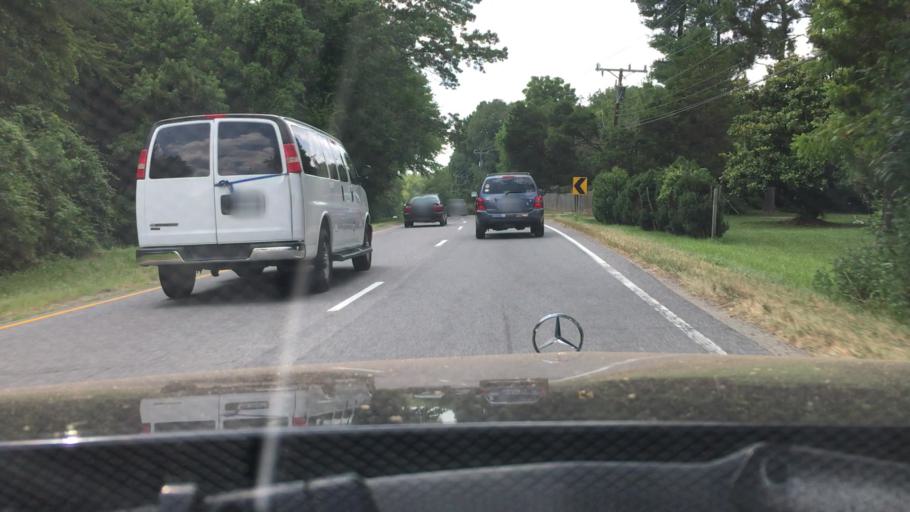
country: US
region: Virginia
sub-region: Spotsylvania County
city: Spotsylvania
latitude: 38.3019
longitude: -77.6157
